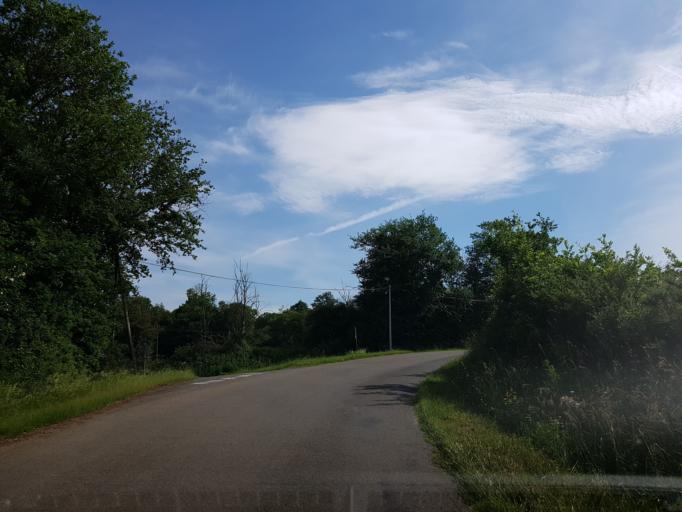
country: FR
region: Poitou-Charentes
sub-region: Departement de la Charente
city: Etagnac
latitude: 45.9337
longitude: 0.7320
